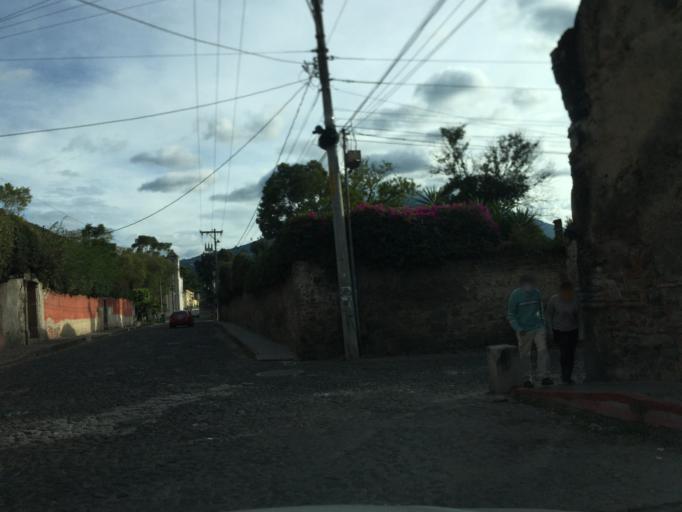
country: GT
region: Sacatepequez
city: Antigua Guatemala
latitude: 14.5525
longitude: -90.7289
